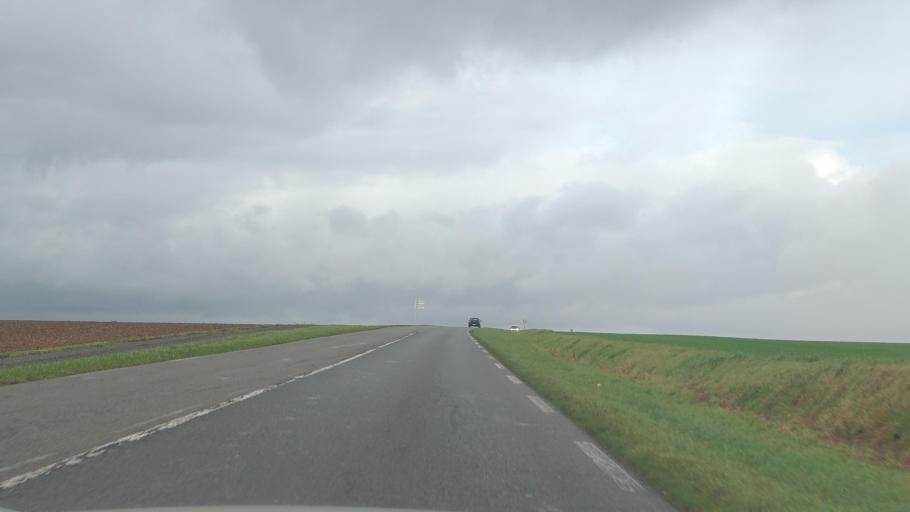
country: FR
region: Picardie
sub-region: Departement de l'Oise
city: Troissereux
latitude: 49.4953
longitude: 2.0259
